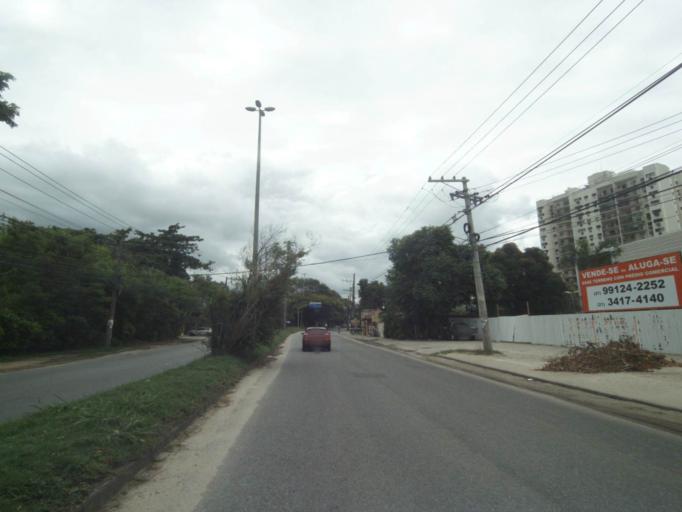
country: BR
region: Rio de Janeiro
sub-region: Nilopolis
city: Nilopolis
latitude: -22.9643
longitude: -43.4059
